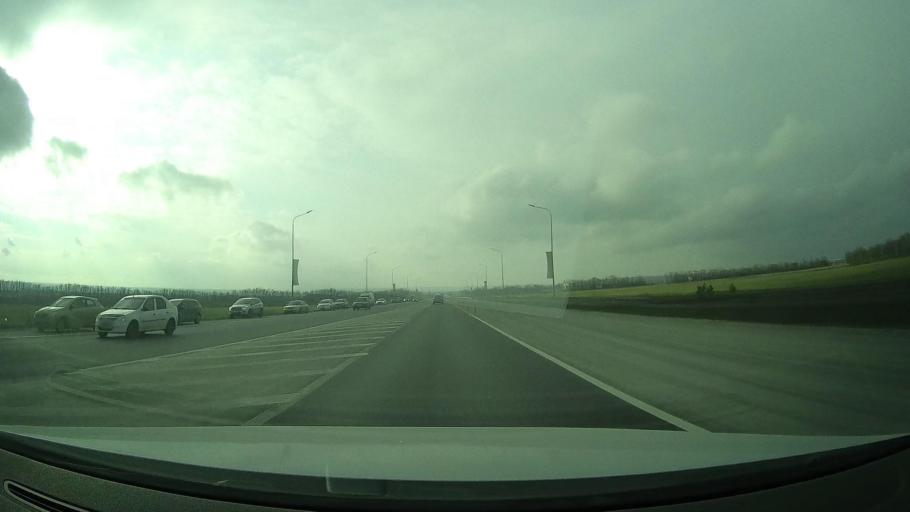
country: RU
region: Rostov
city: Grushevskaya
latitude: 47.4783
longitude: 39.9192
